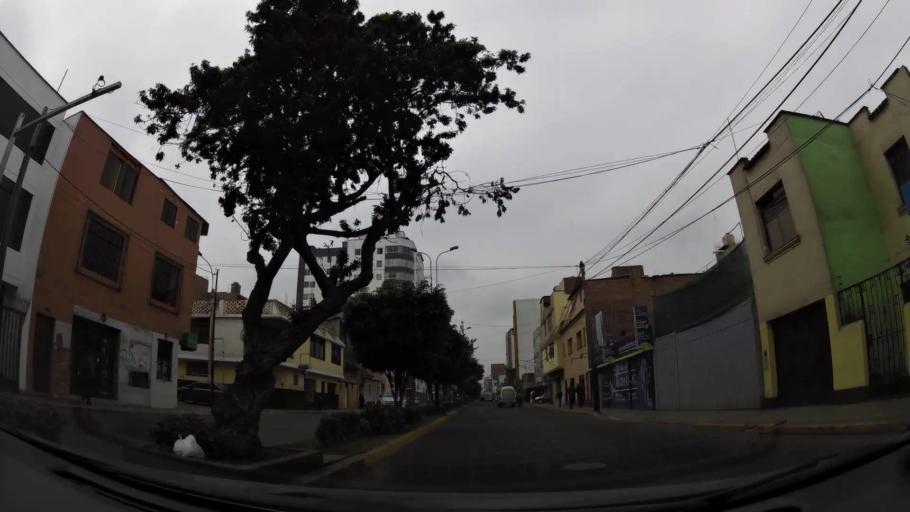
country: PE
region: Lima
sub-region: Lima
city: San Isidro
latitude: -12.0851
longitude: -77.0454
